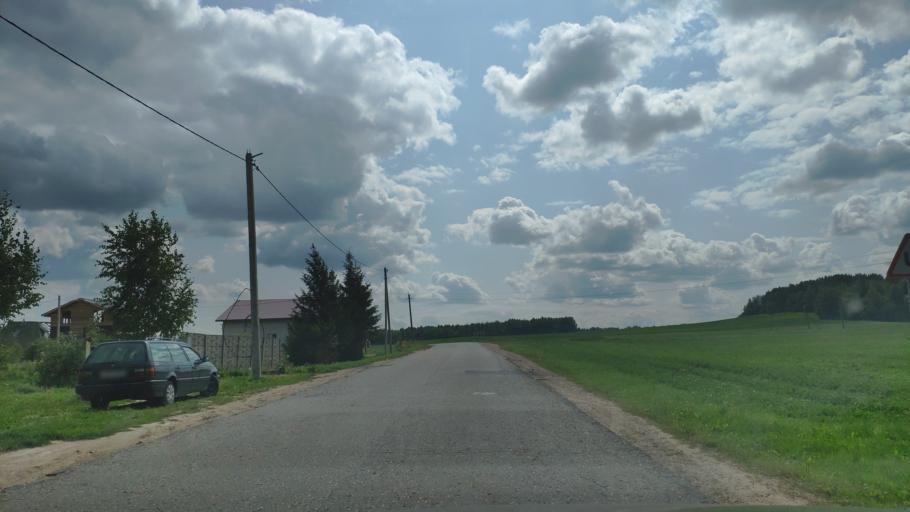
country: BY
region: Minsk
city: Khatsyezhyna
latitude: 53.8561
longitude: 27.3063
